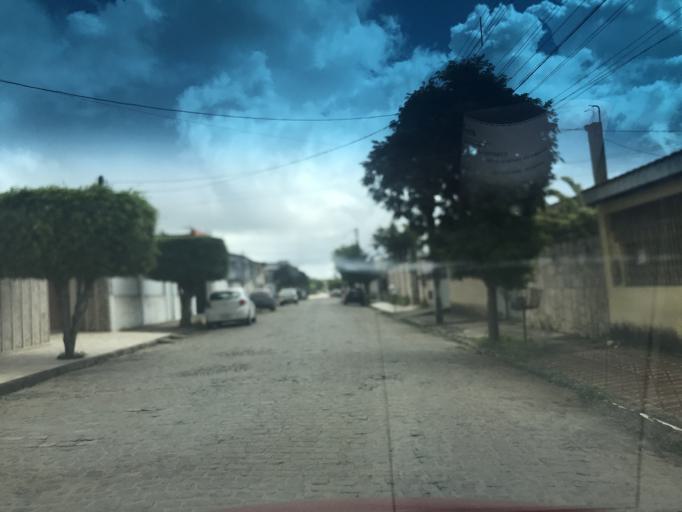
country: BR
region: Bahia
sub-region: Cruz Das Almas
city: Cruz das Almas
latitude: -12.6771
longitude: -39.0985
